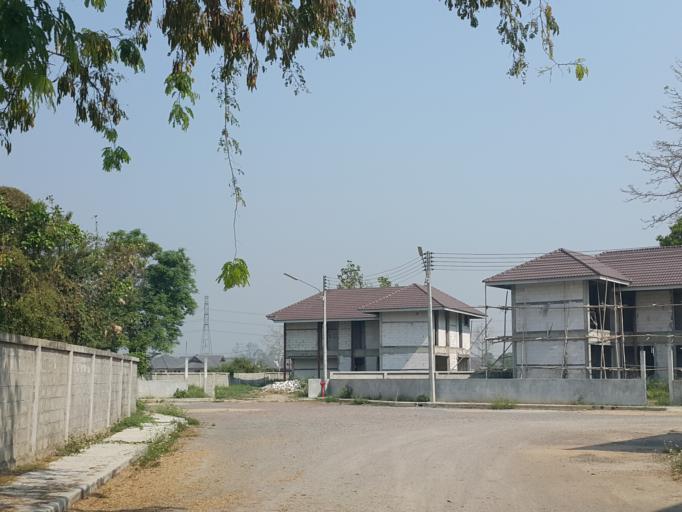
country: TH
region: Chiang Mai
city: Hang Dong
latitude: 18.7156
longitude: 98.9609
